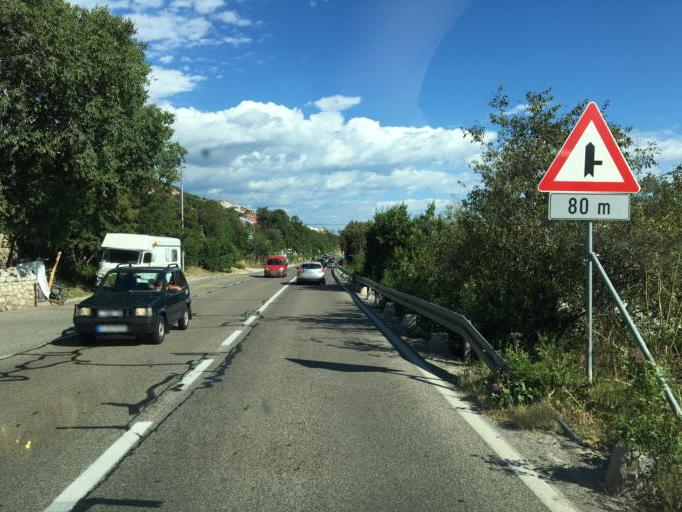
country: HR
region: Primorsko-Goranska
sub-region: Grad Crikvenica
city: Jadranovo
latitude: 45.2105
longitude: 14.6530
